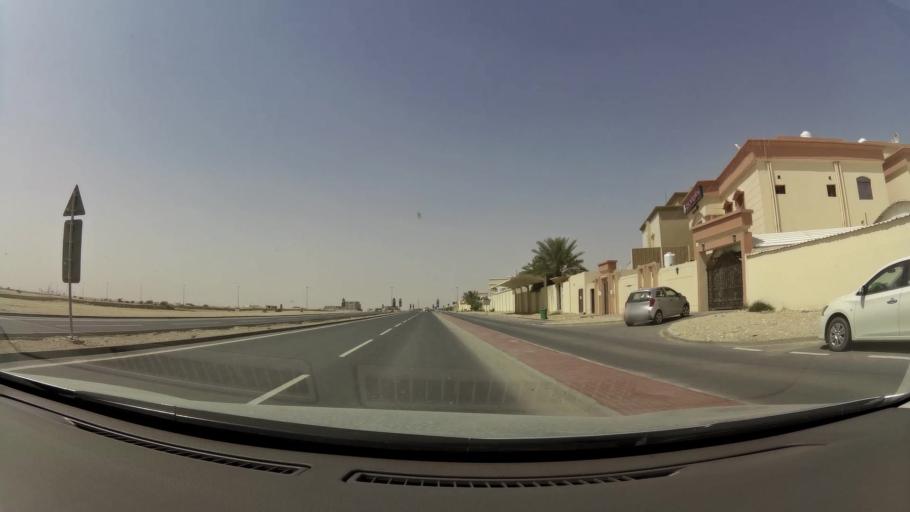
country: QA
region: Baladiyat Umm Salal
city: Umm Salal Muhammad
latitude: 25.3677
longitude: 51.4244
